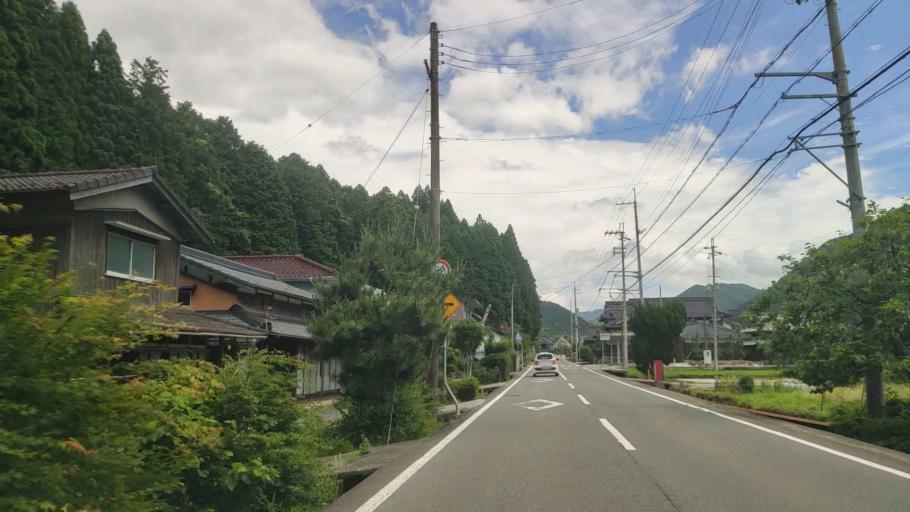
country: JP
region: Hyogo
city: Nishiwaki
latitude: 35.1634
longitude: 134.9288
